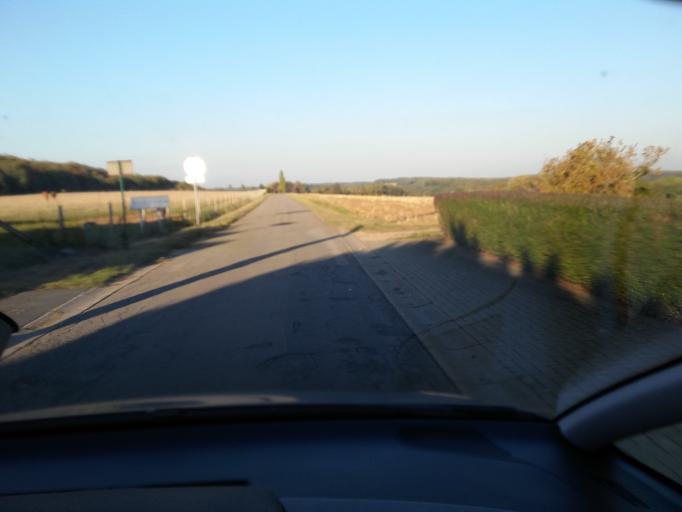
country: BE
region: Wallonia
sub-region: Province du Luxembourg
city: Arlon
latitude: 49.6942
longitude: 5.8392
